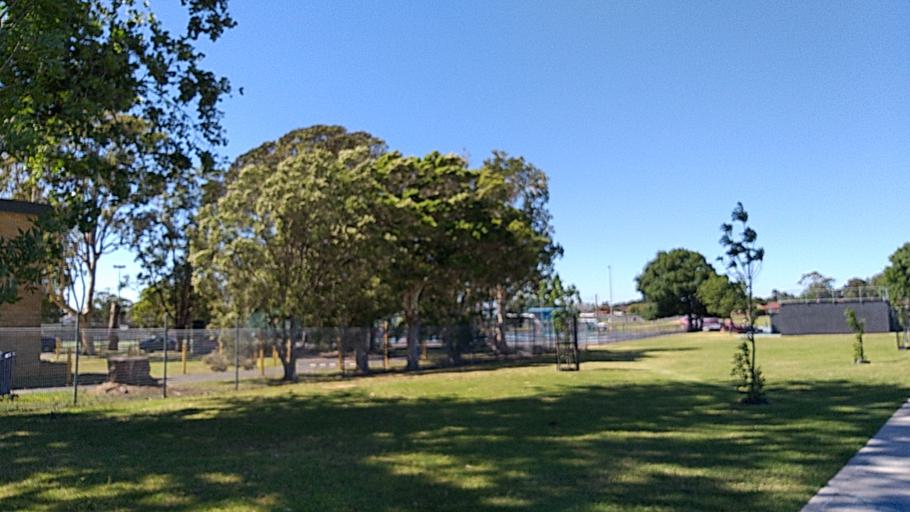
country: AU
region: New South Wales
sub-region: Wollongong
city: Fairy Meadow
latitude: -34.3906
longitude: 150.8909
